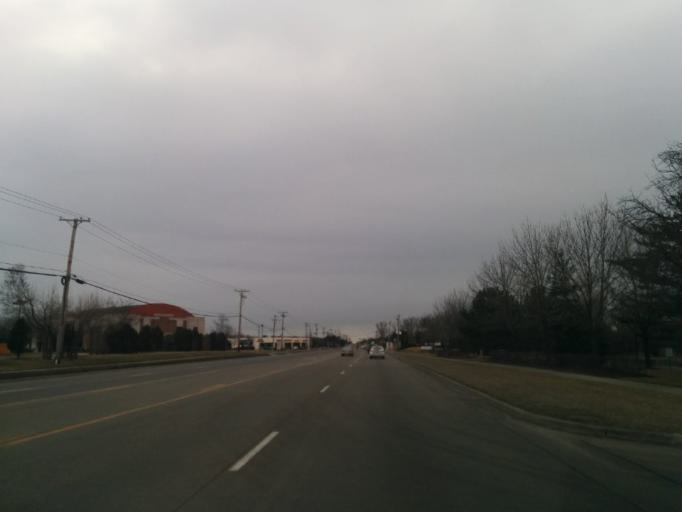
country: US
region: Illinois
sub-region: Cook County
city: Northbrook
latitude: 42.0936
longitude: -87.8767
